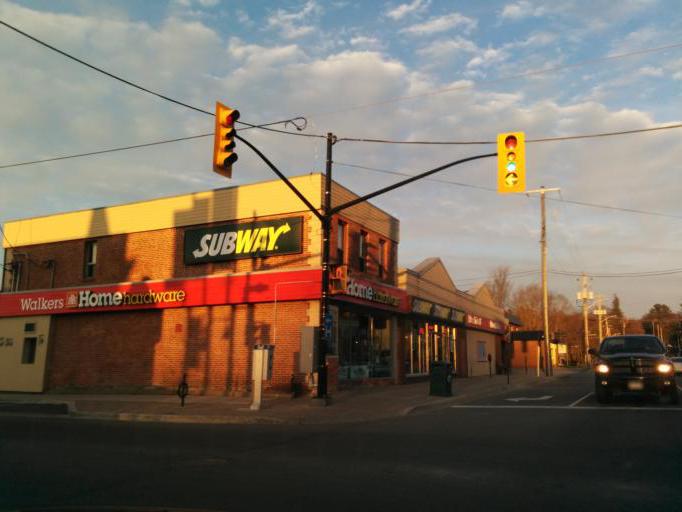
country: CA
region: Ontario
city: Bancroft
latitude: 45.0464
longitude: -78.5087
